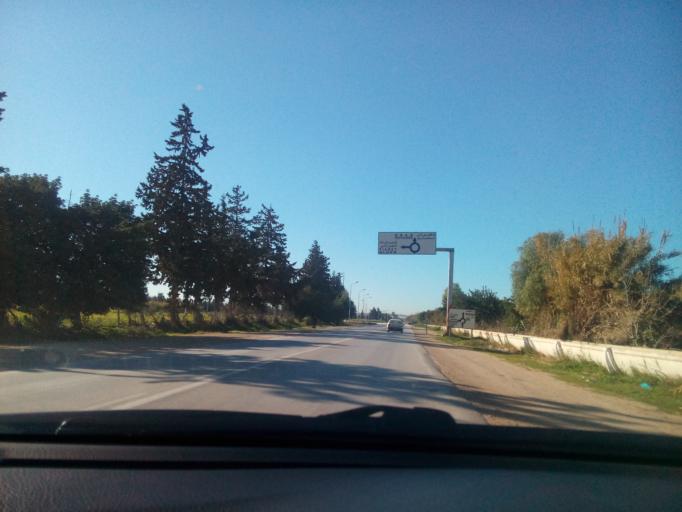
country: DZ
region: Relizane
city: Relizane
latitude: 35.7218
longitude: 0.5104
